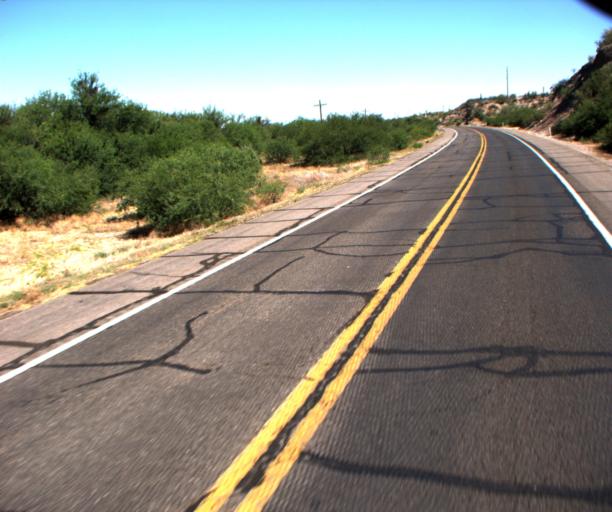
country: US
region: Arizona
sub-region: Pinal County
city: Mammoth
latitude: 32.7511
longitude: -110.6464
